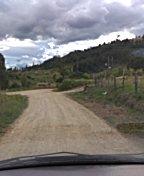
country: CO
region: Boyaca
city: Paipa
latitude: 5.8169
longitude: -73.0902
